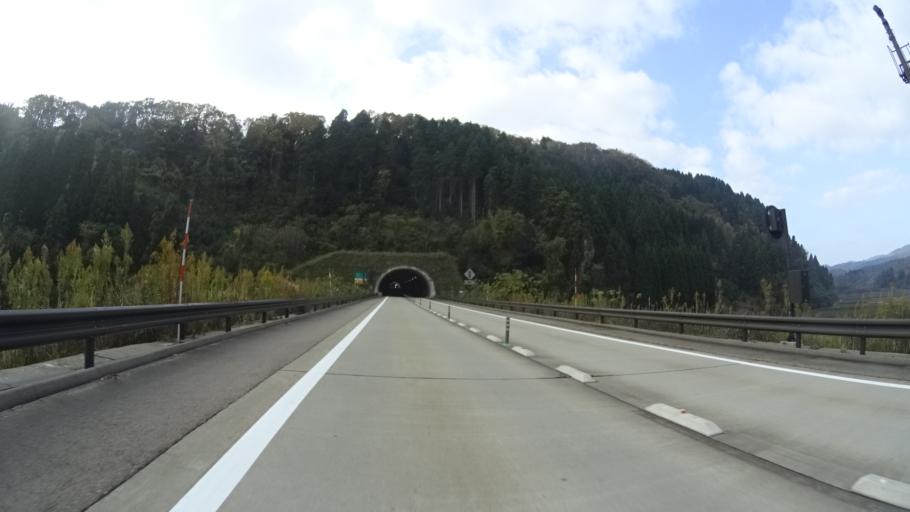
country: JP
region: Toyama
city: Himi
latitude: 36.9414
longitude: 137.0213
